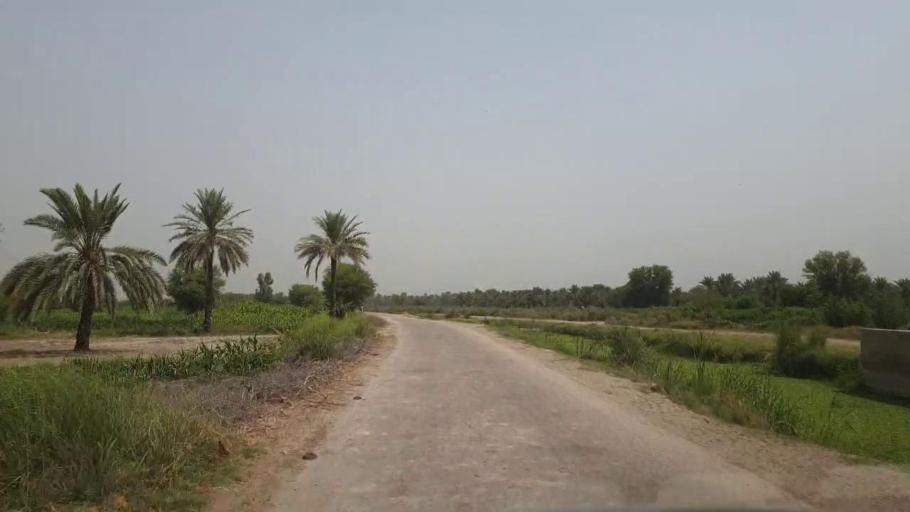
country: PK
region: Sindh
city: Gambat
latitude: 27.4309
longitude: 68.5607
